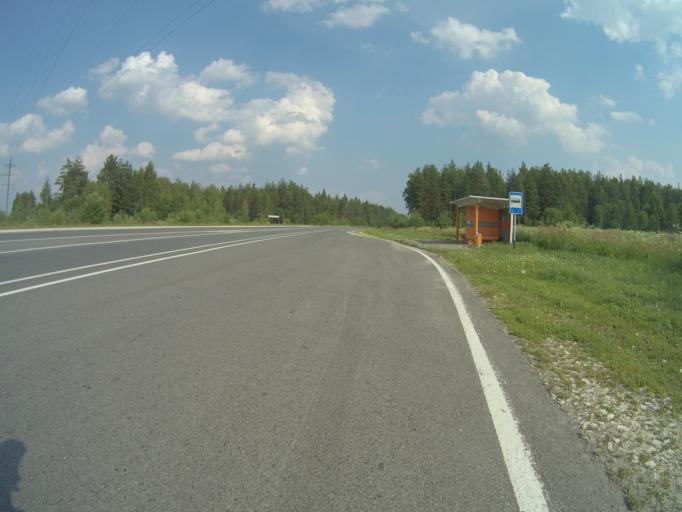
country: RU
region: Vladimir
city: Andreyevo
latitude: 55.9351
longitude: 41.0975
